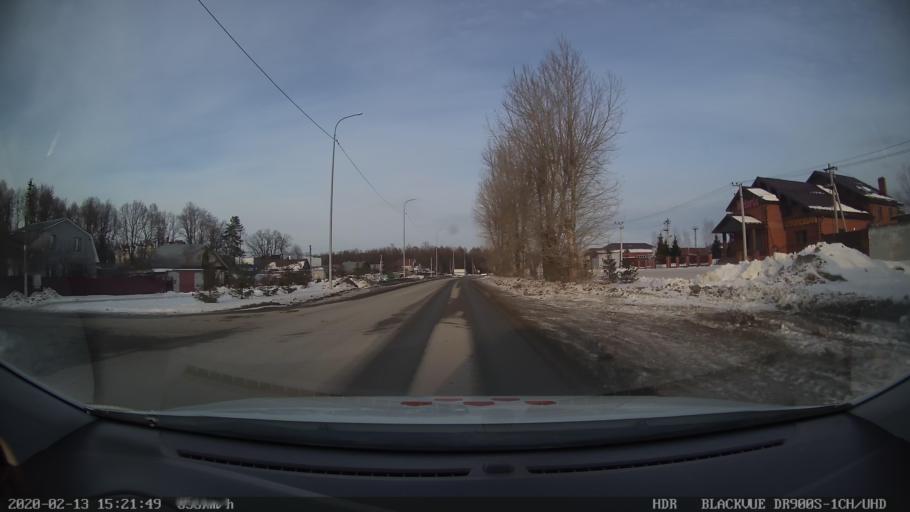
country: RU
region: Tatarstan
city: Vysokaya Gora
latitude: 55.9204
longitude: 49.3034
